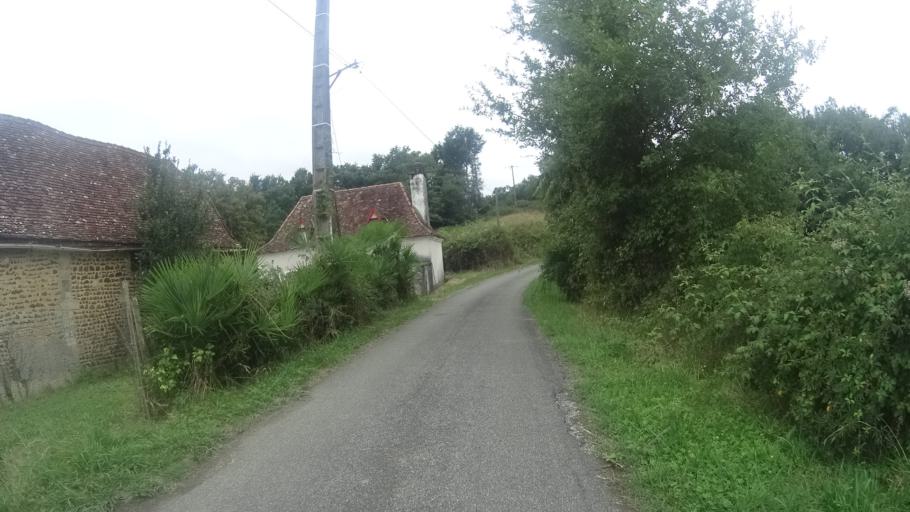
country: FR
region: Aquitaine
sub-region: Departement des Pyrenees-Atlantiques
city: Mont
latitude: 43.4843
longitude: -0.6900
